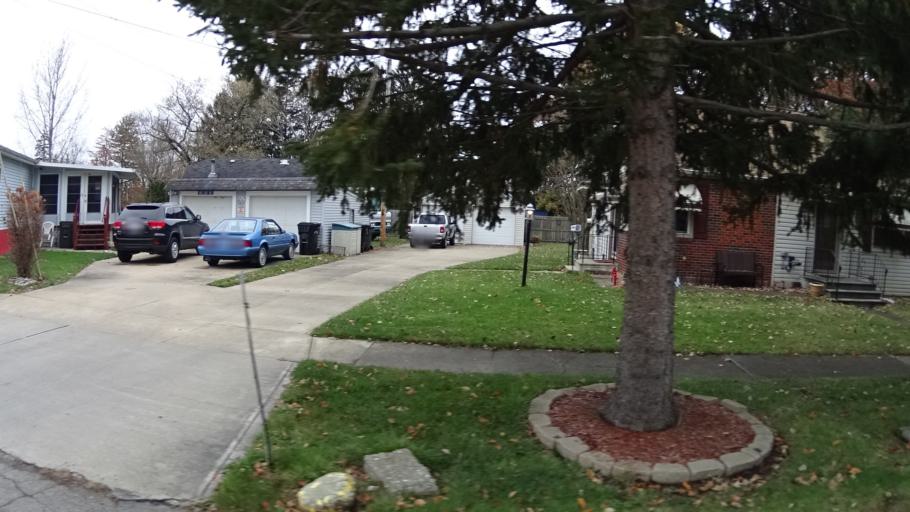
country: US
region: Ohio
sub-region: Lorain County
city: Elyria
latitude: 41.3467
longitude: -82.1134
